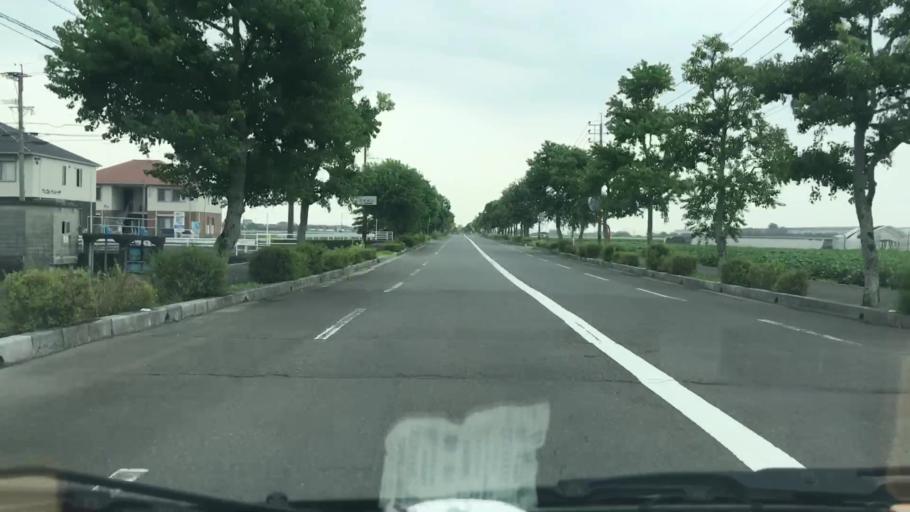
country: JP
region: Saga Prefecture
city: Saga-shi
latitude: 33.2071
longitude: 130.3036
